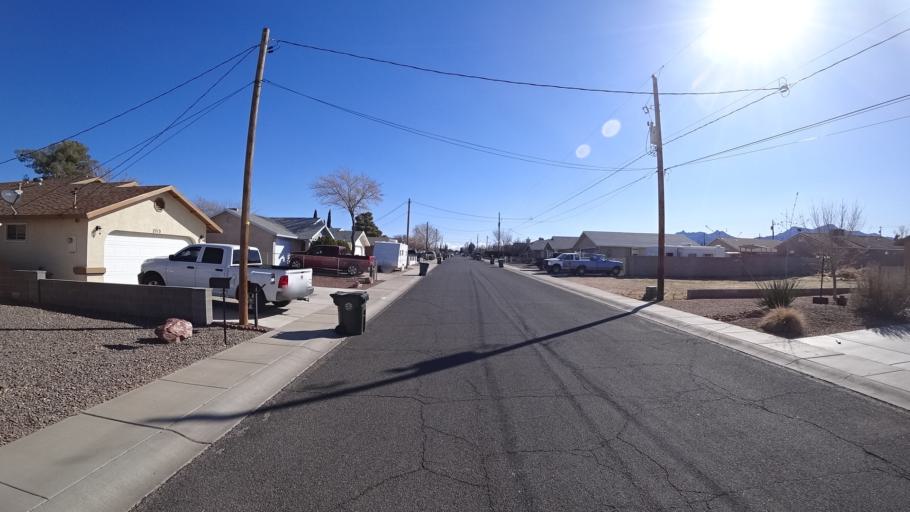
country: US
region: Arizona
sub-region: Mohave County
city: Kingman
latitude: 35.2007
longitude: -114.0154
